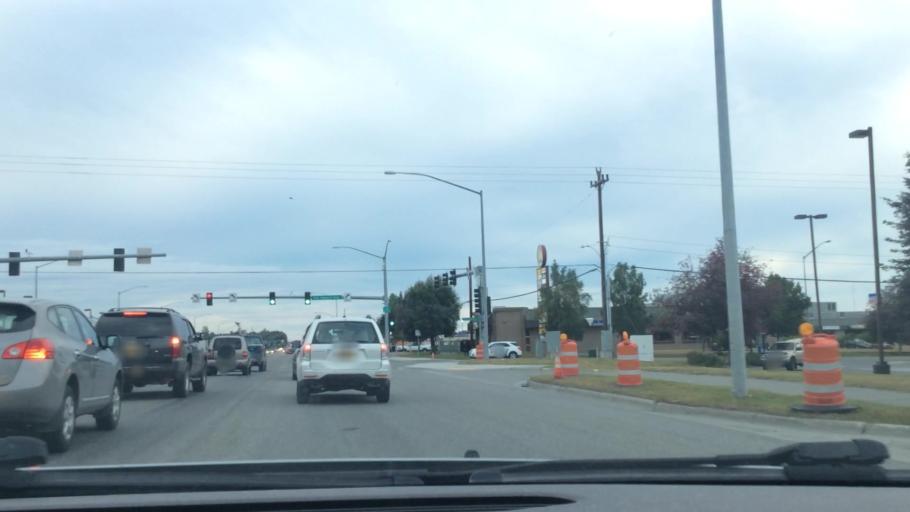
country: US
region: Alaska
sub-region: Anchorage Municipality
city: Anchorage
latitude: 61.1808
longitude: -149.8667
